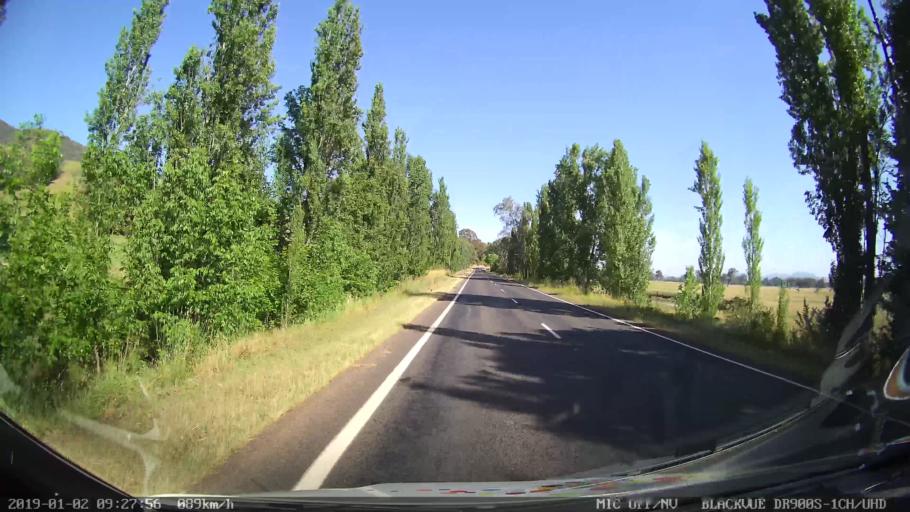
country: AU
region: New South Wales
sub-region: Tumut Shire
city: Tumut
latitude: -35.3566
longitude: 148.2530
